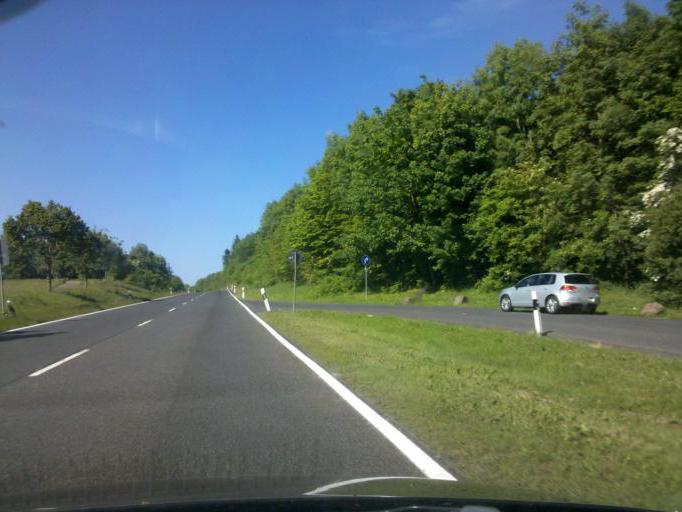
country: DE
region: Rheinland-Pfalz
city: Bretthausen
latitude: 50.6705
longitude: 8.0597
